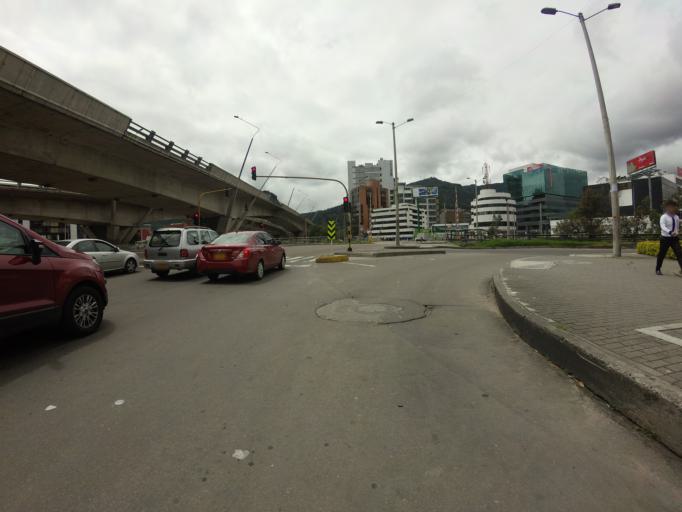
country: CO
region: Bogota D.C.
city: Barrio San Luis
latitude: 4.6850
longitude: -74.0490
